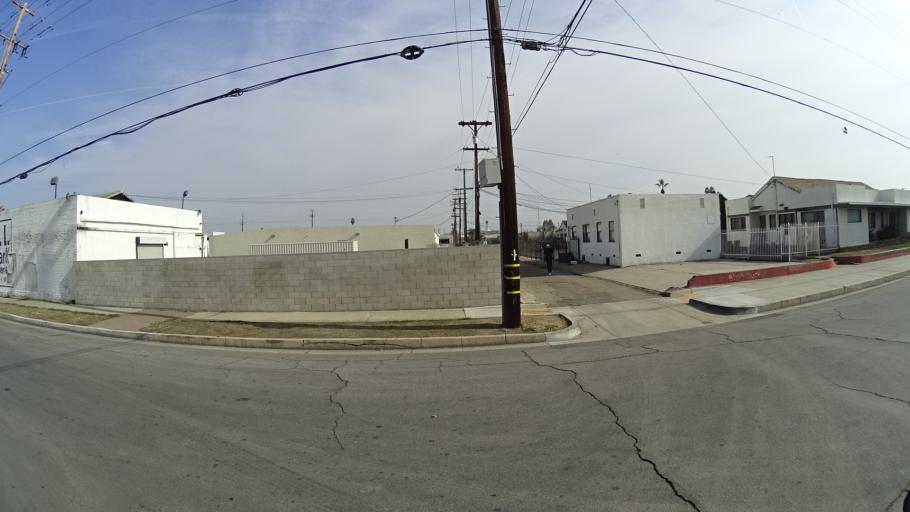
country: US
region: California
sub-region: Kern County
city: Bakersfield
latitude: 35.3757
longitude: -119.0049
